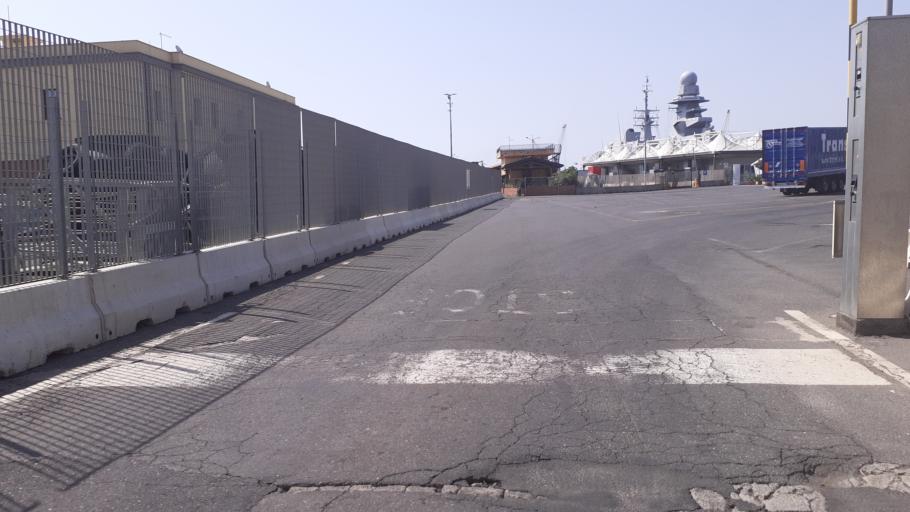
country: IT
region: Sicily
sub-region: Catania
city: Catania
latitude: 37.4984
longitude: 15.0947
